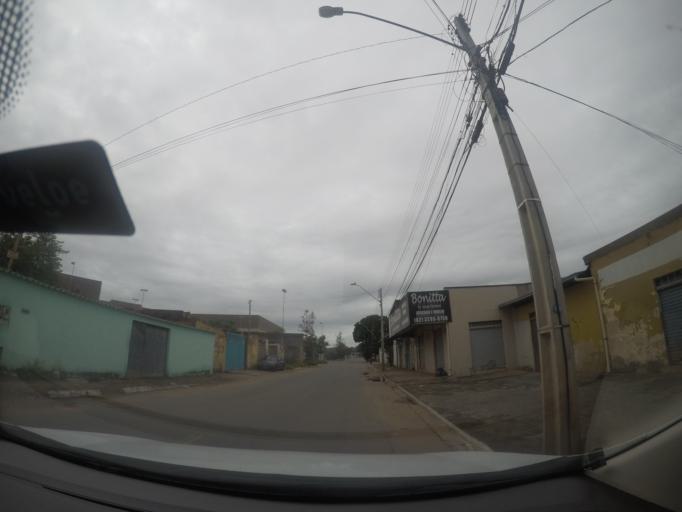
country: BR
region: Goias
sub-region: Goiania
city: Goiania
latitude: -16.6650
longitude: -49.3099
